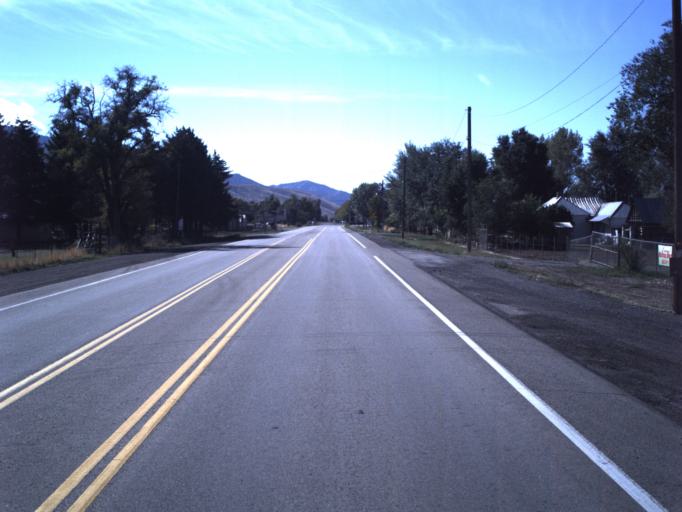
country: US
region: Utah
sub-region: Juab County
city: Nephi
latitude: 39.5630
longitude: -111.8619
